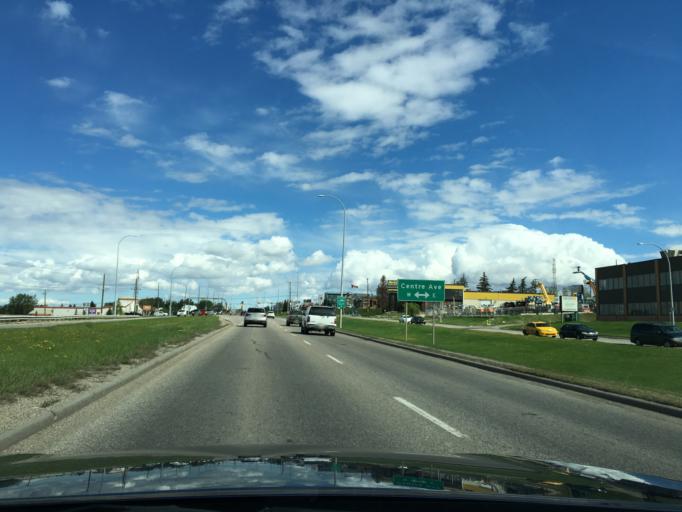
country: CA
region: Alberta
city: Calgary
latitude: 51.0502
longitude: -114.0016
